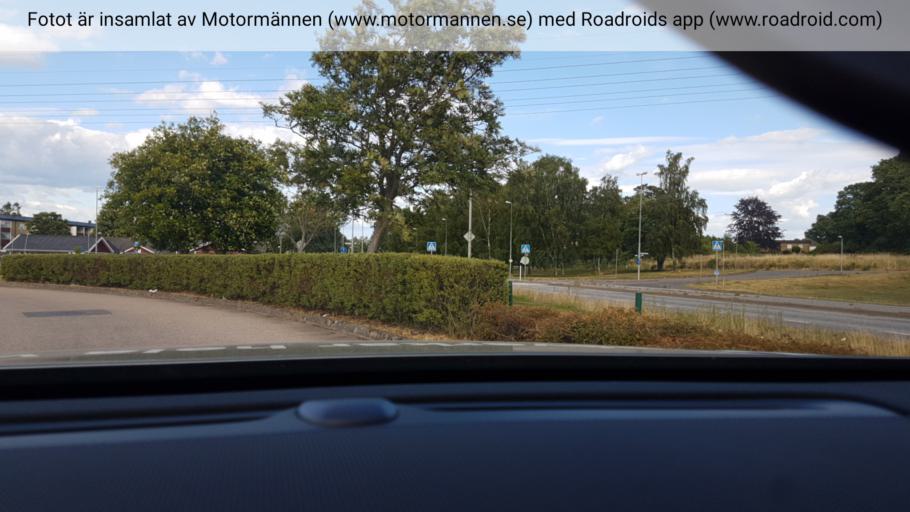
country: SE
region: Skane
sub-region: Hassleholms Kommun
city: Hassleholm
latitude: 56.1672
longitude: 13.7891
